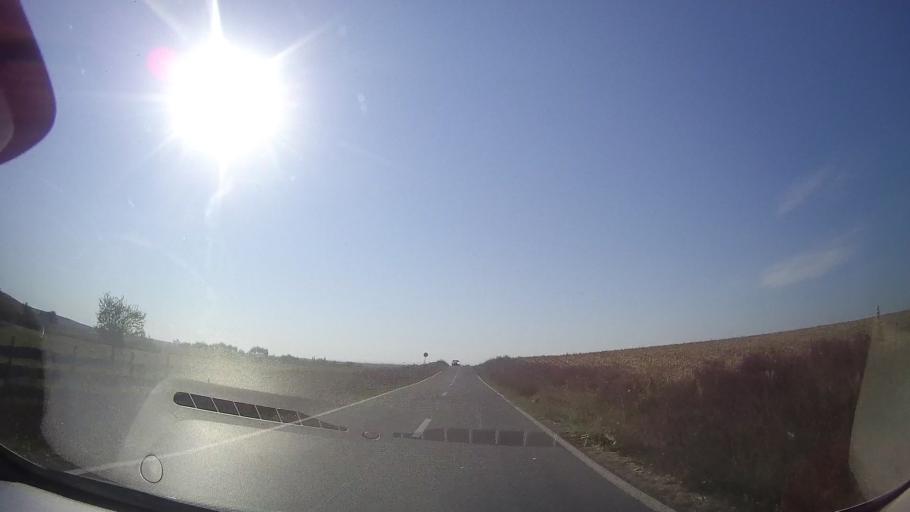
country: RO
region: Timis
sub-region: Comuna Topolovatu Mare
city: Topolovatu Mare
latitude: 45.8008
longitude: 21.5860
